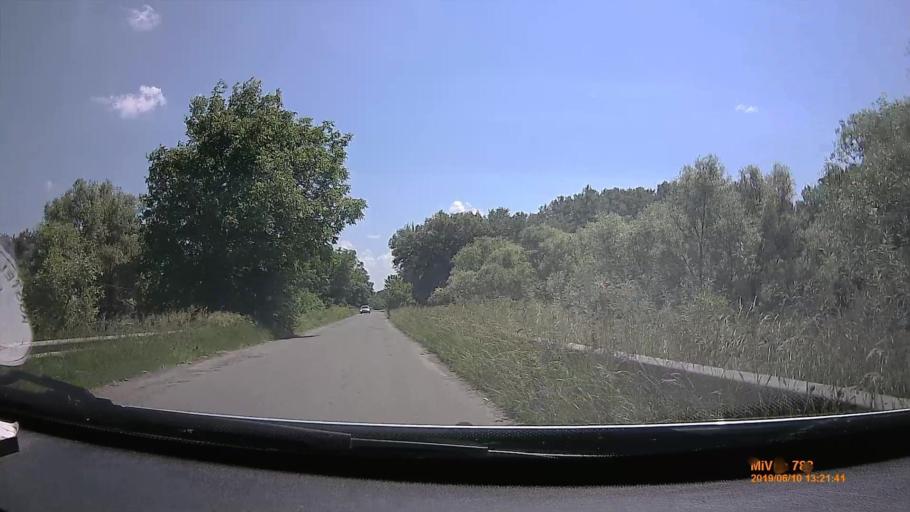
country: HU
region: Borsod-Abauj-Zemplen
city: Tiszaluc
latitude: 48.0347
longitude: 21.0774
